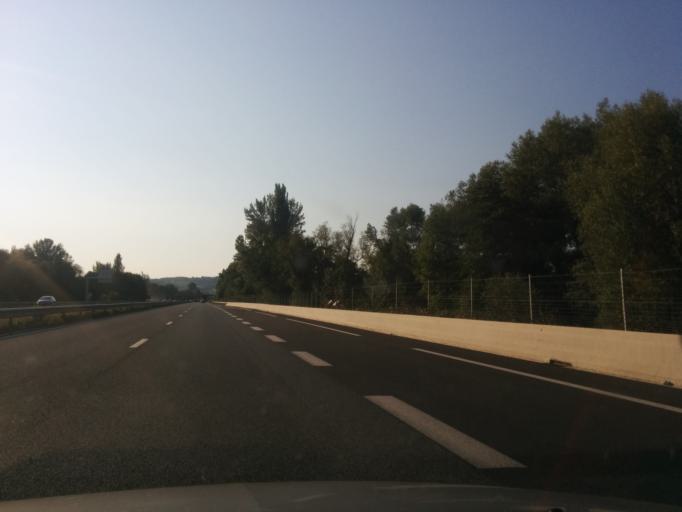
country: FR
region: Rhone-Alpes
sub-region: Departement de l'Isere
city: Saint-Jean-de-Moirans
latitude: 45.3253
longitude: 5.5998
